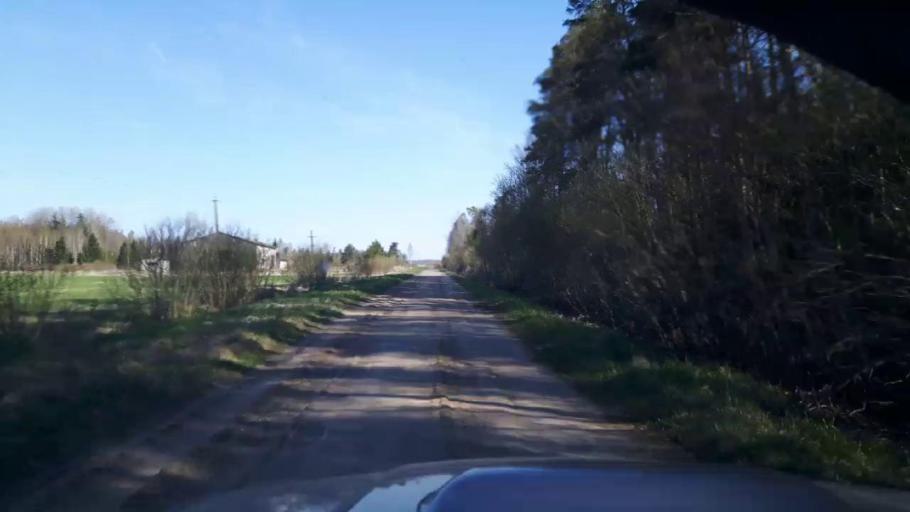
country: EE
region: Paernumaa
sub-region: Vaendra vald (alev)
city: Vandra
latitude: 58.5171
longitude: 24.9605
